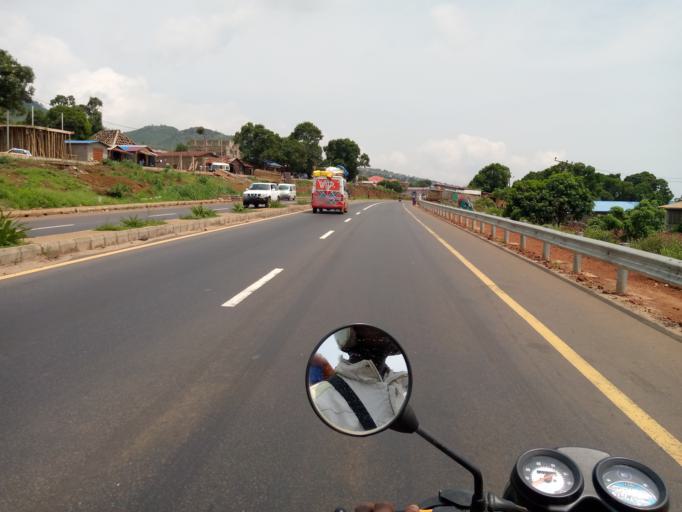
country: SL
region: Western Area
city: Waterloo
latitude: 8.3647
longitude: -13.0861
